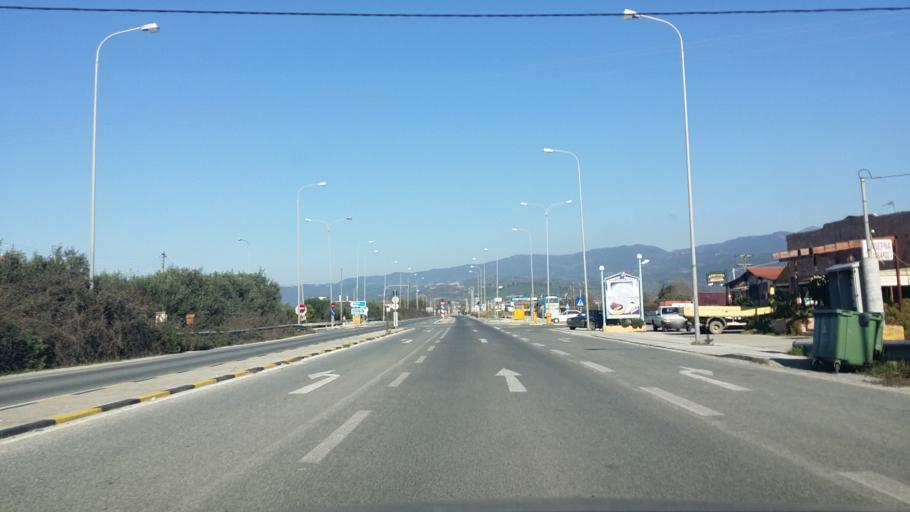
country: GR
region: West Greece
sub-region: Nomos Aitolias kai Akarnanias
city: Krikellos
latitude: 38.9294
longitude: 21.1773
